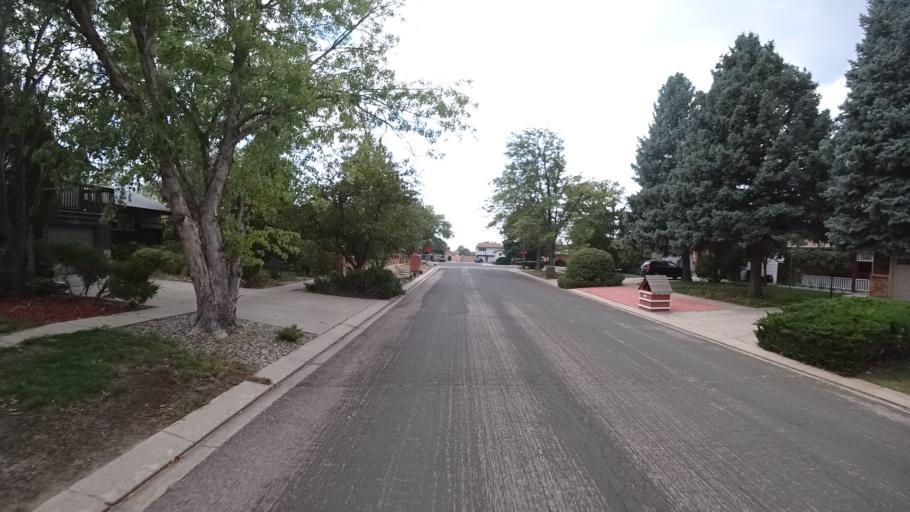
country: US
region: Colorado
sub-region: El Paso County
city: Colorado Springs
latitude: 38.8490
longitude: -104.7625
